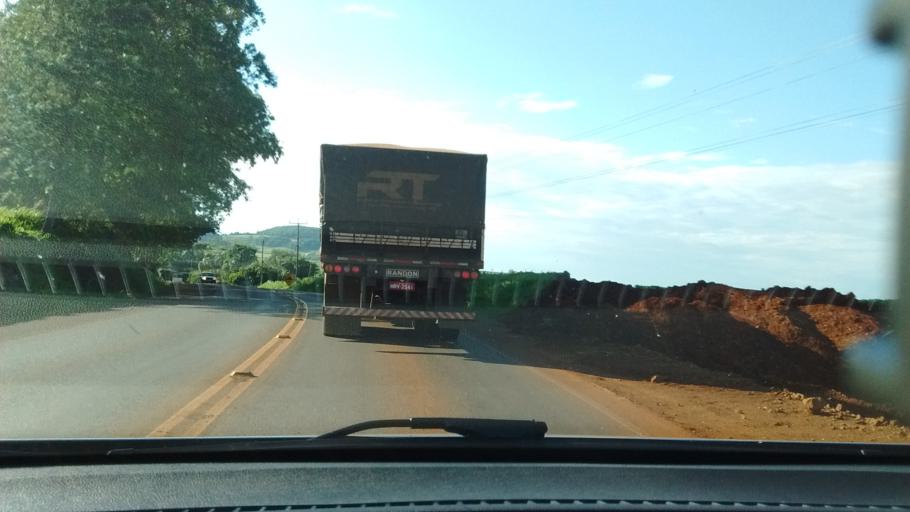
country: BR
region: Parana
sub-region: Cascavel
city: Cascavel
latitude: -25.2210
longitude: -53.5952
